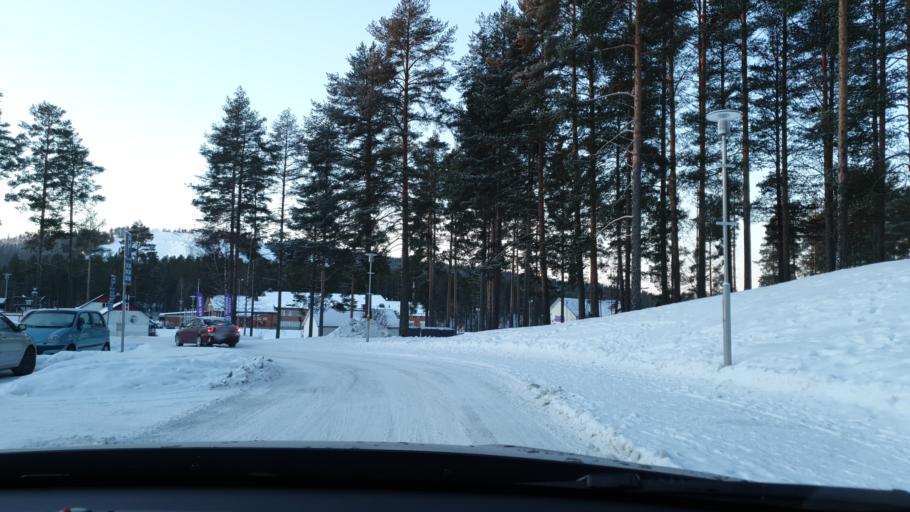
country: FI
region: Kainuu
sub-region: Kajaani
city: Vuokatti
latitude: 64.1387
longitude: 28.2868
